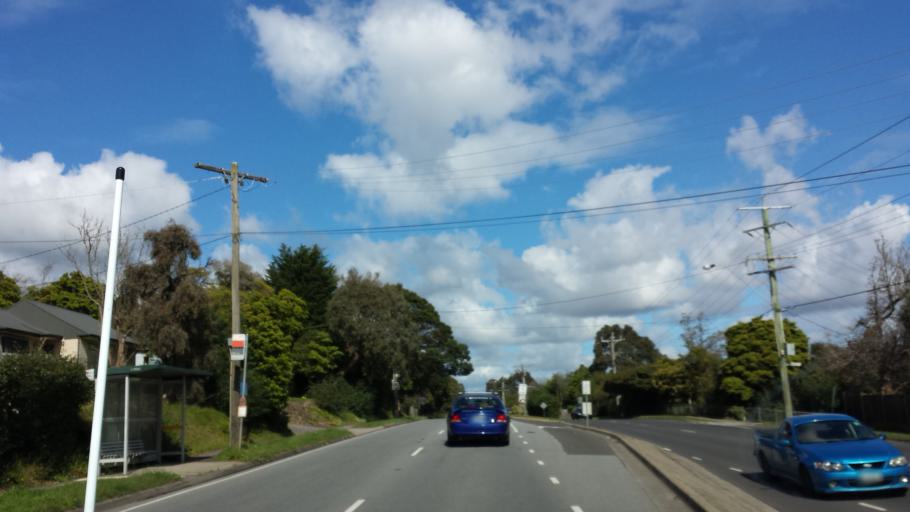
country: AU
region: Victoria
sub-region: Knox
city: Boronia
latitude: -37.8521
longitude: 145.2862
